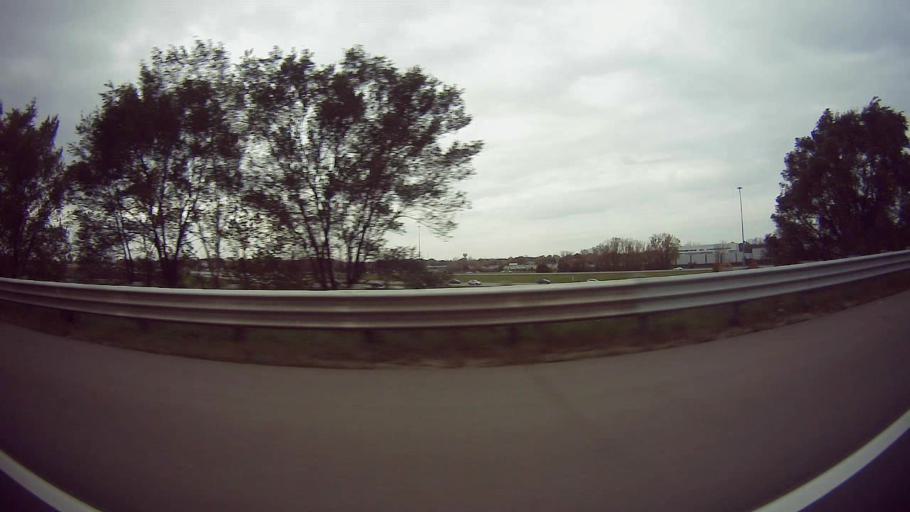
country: US
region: Michigan
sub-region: Wayne County
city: Plymouth
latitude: 42.3891
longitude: -83.4338
